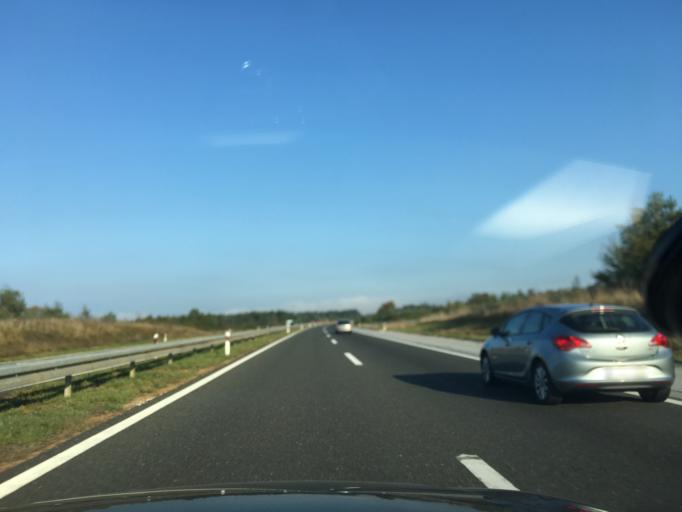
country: HR
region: Licko-Senjska
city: Gospic
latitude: 44.5323
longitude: 15.4460
